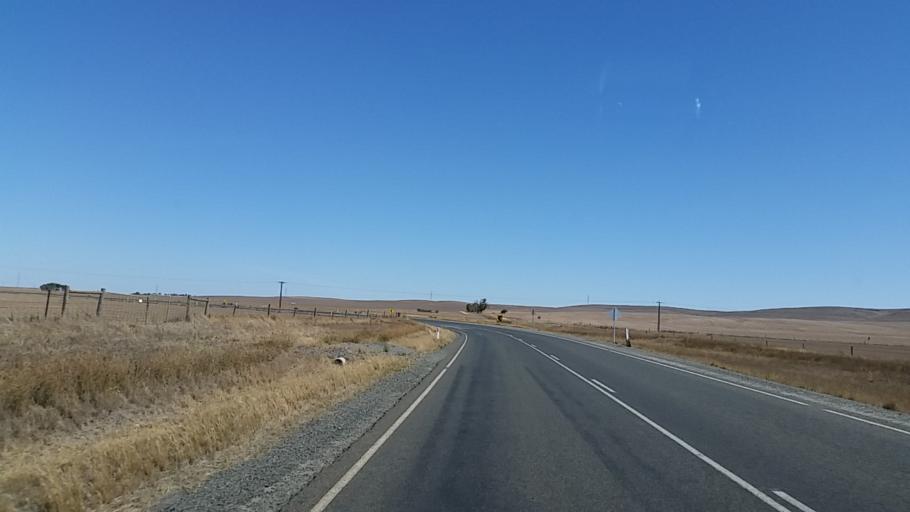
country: AU
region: South Australia
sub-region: Clare and Gilbert Valleys
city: Clare
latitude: -33.6825
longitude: 138.9077
